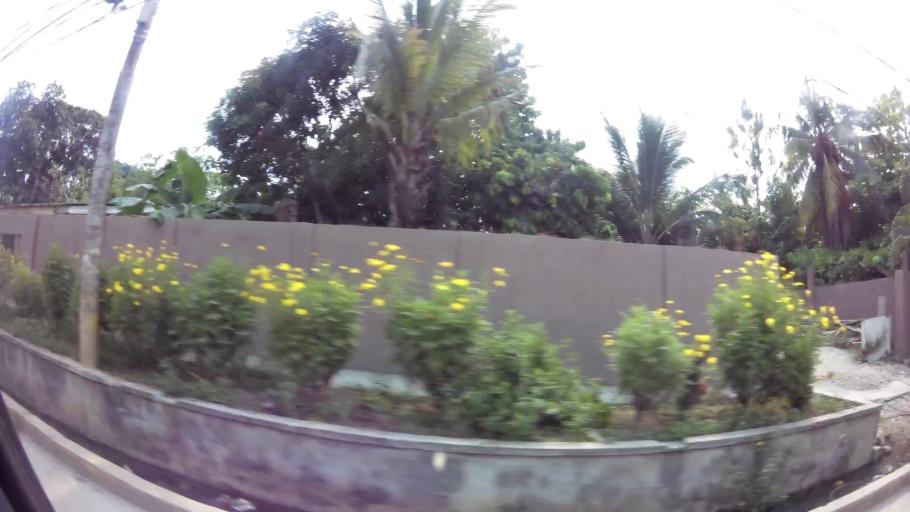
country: HN
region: Atlantida
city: El Triunfo de la Cruz
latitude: 15.7753
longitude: -87.4491
